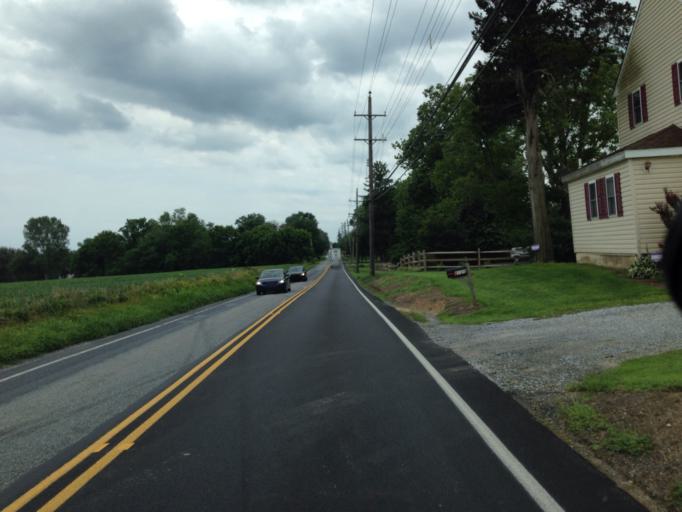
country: US
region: Pennsylvania
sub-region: Chester County
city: West Grove
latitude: 39.7917
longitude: -75.8845
